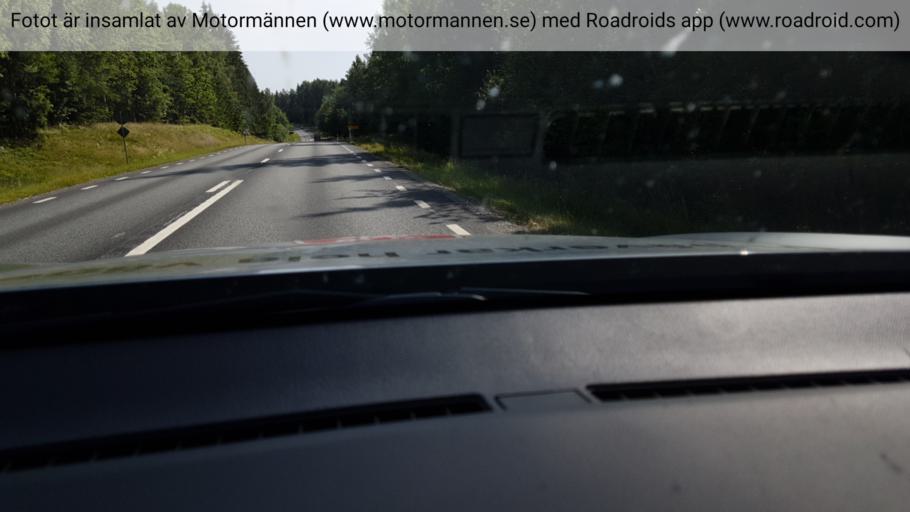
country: SE
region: Joenkoeping
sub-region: Aneby Kommun
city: Aneby
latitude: 57.9075
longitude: 14.8969
